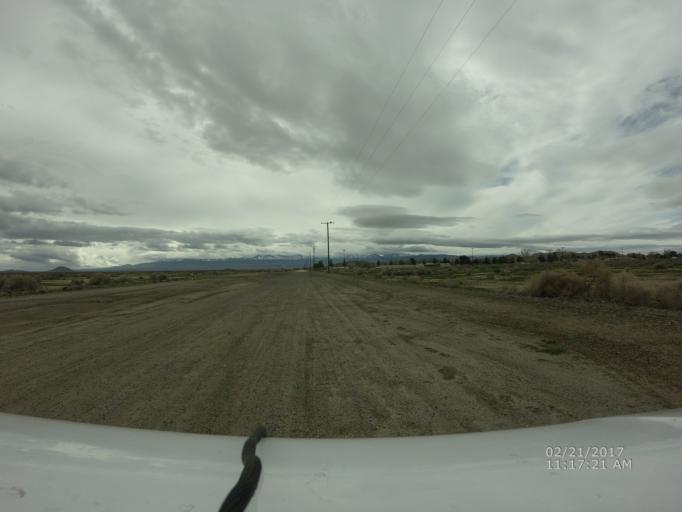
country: US
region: California
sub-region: Los Angeles County
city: Lake Los Angeles
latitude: 34.6327
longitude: -117.8094
